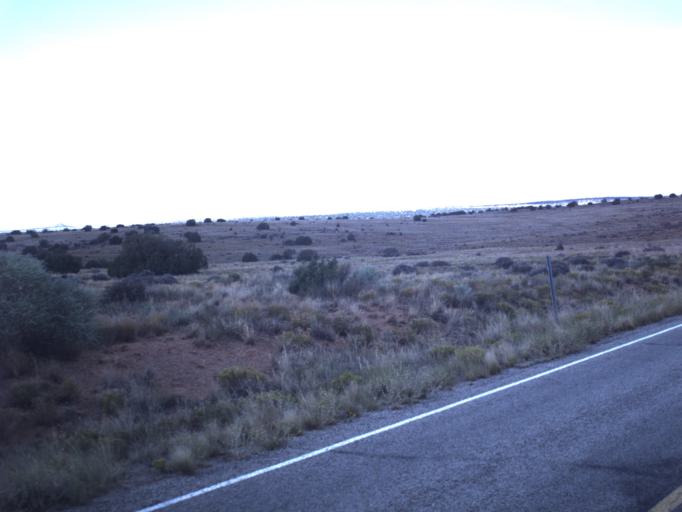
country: US
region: Utah
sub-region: Grand County
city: Moab
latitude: 38.4950
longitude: -109.7347
